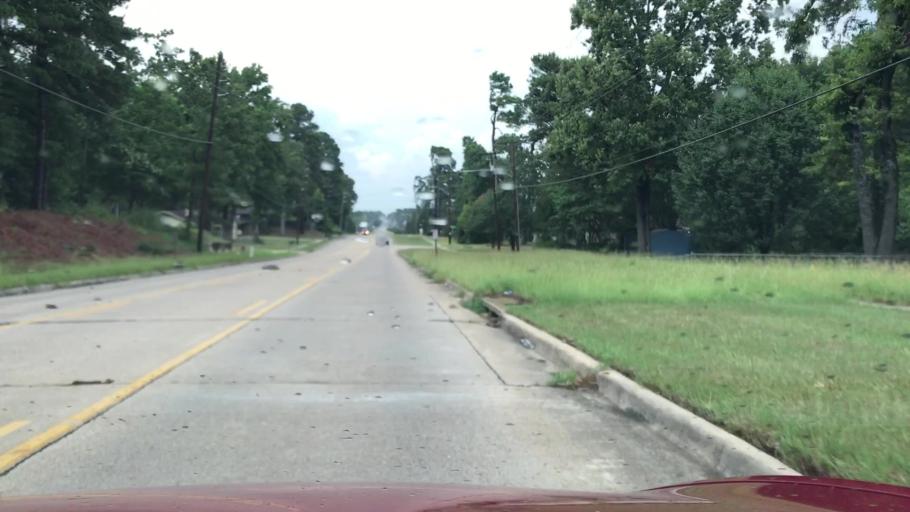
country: US
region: Louisiana
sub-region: De Soto Parish
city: Stonewall
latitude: 32.3962
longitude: -93.7804
